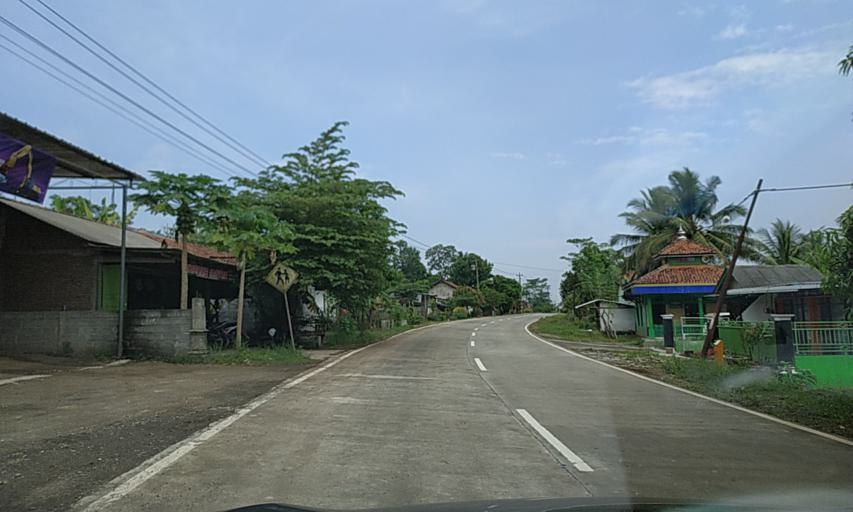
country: ID
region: Central Java
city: Ciloning
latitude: -7.4803
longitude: 108.8431
